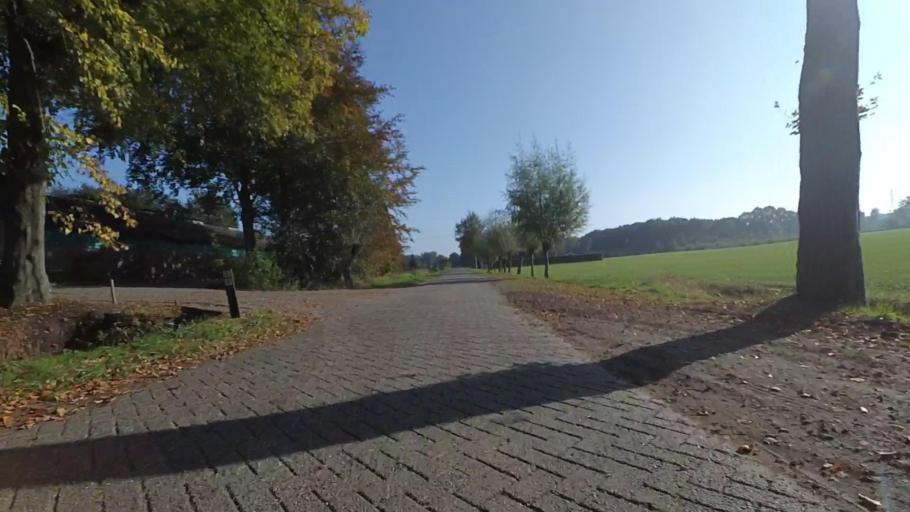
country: NL
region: Gelderland
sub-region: Gemeente Nijkerk
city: Nijkerk
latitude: 52.2511
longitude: 5.5379
